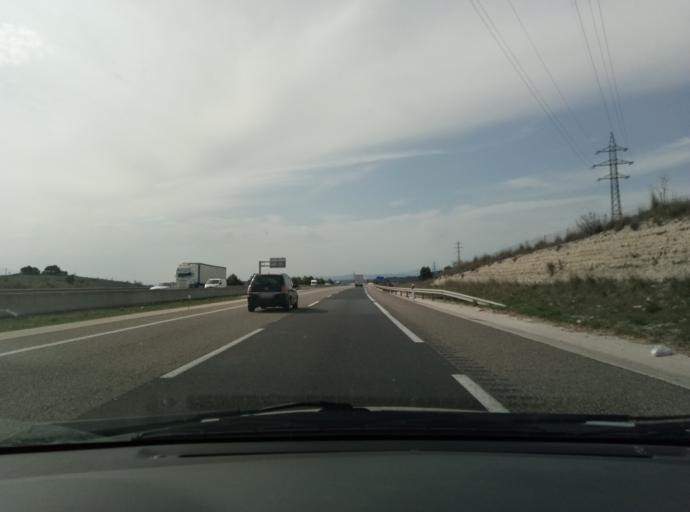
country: ES
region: Catalonia
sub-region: Provincia de Lleida
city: Sant Guim de Freixenet
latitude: 41.6250
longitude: 1.3779
